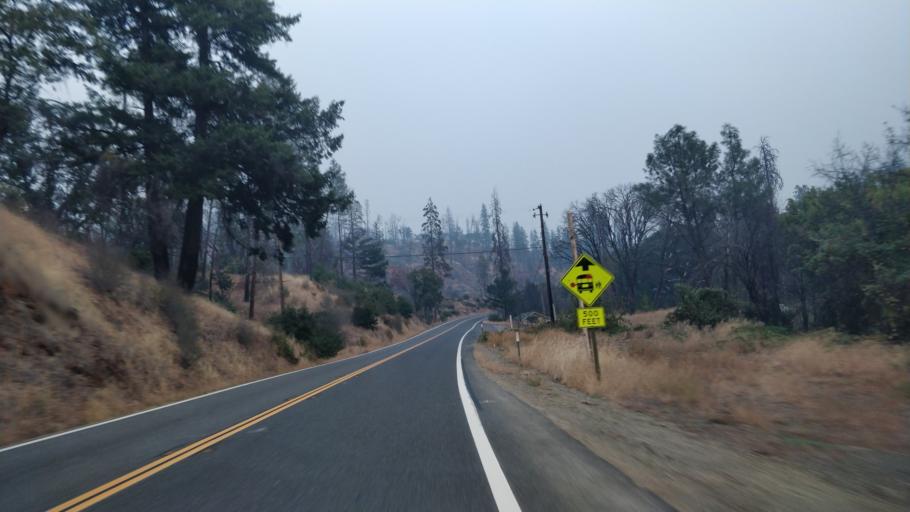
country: US
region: California
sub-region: Trinity County
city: Weaverville
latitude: 40.7665
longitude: -123.1044
